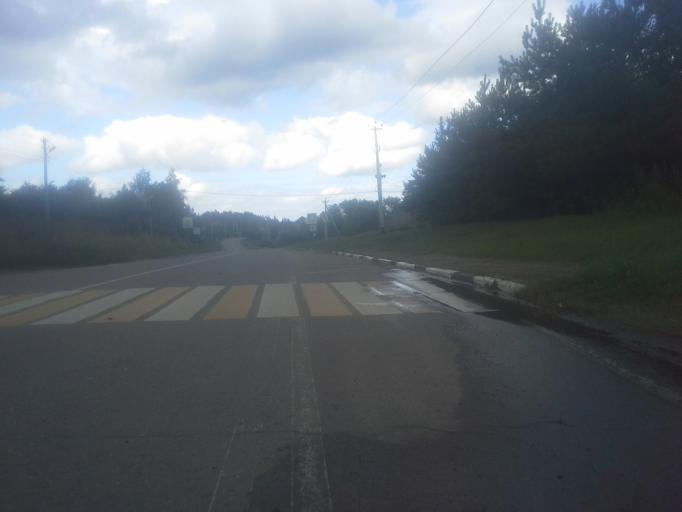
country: RU
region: Moskovskaya
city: Karinskoye
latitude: 55.6563
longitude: 36.6257
